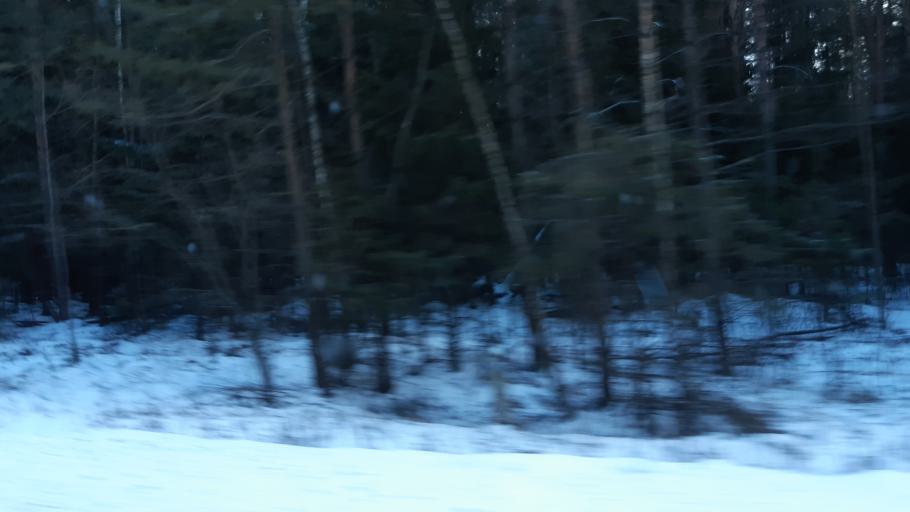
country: RU
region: Moskovskaya
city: Noginsk-9
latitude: 56.0726
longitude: 38.5662
